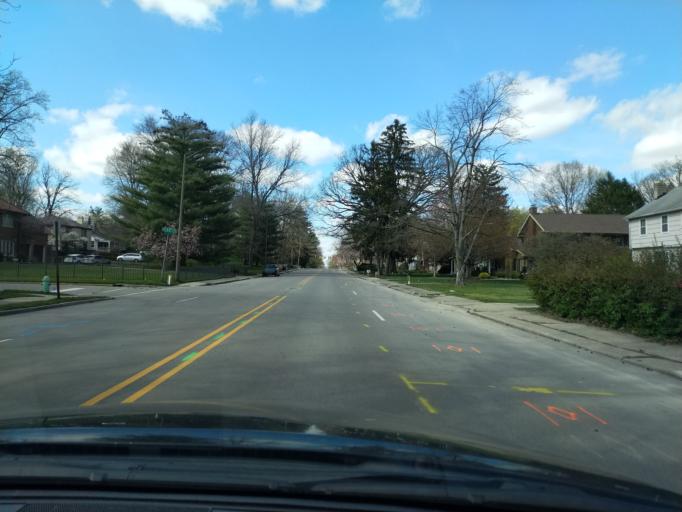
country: US
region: Indiana
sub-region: Marion County
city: Broad Ripple
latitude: 39.8521
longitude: -86.1501
